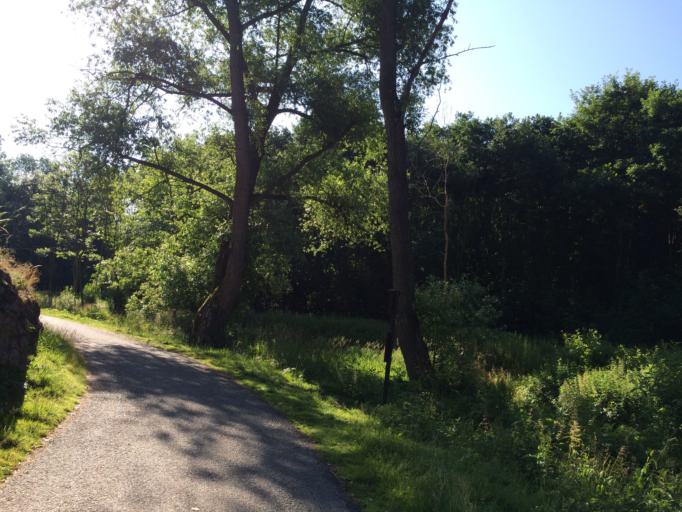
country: CZ
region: Central Bohemia
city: Horomerice
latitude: 50.0946
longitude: 14.3216
